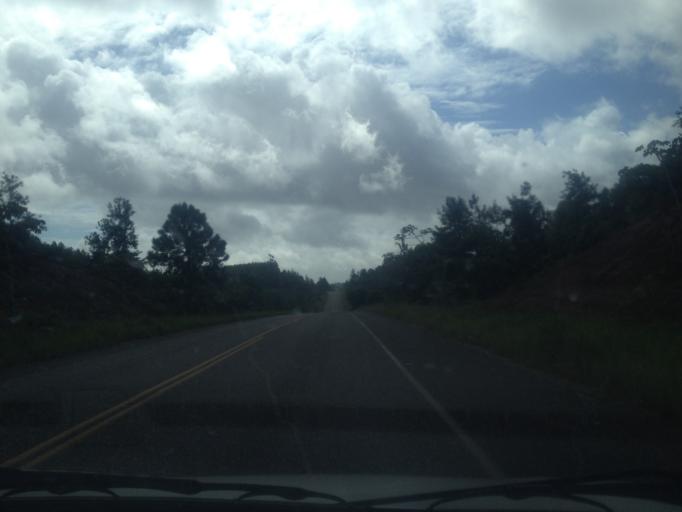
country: BR
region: Bahia
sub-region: Entre Rios
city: Entre Rios
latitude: -12.1635
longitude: -37.8071
